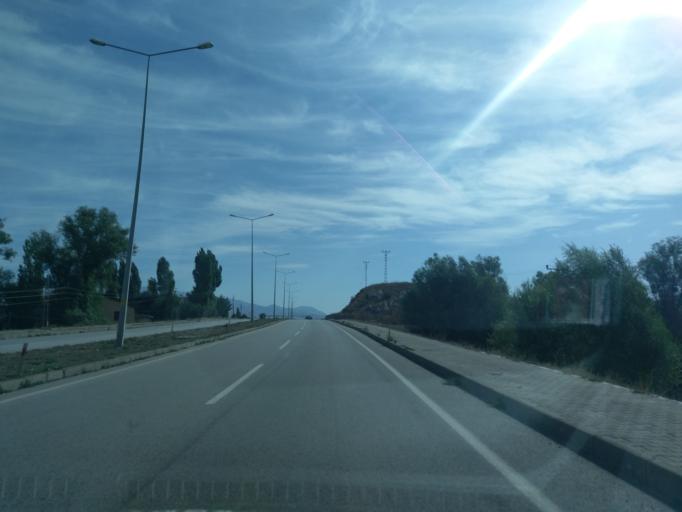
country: TR
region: Sivas
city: Imranli
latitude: 39.8705
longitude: 38.1240
